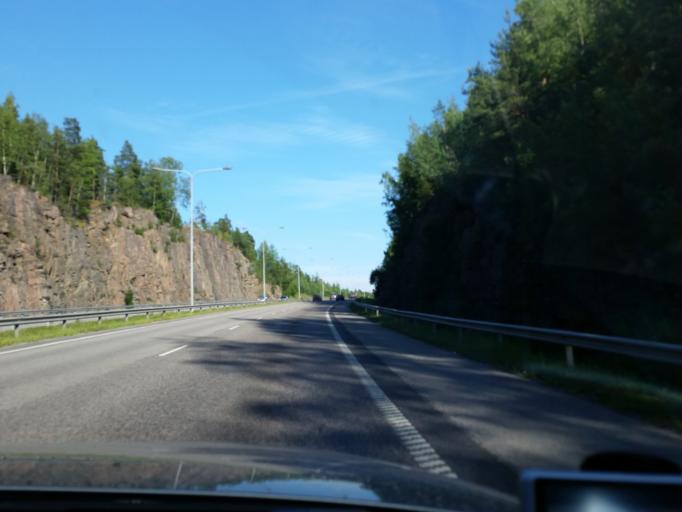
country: FI
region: Uusimaa
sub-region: Helsinki
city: Espoo
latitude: 60.2100
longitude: 24.6817
